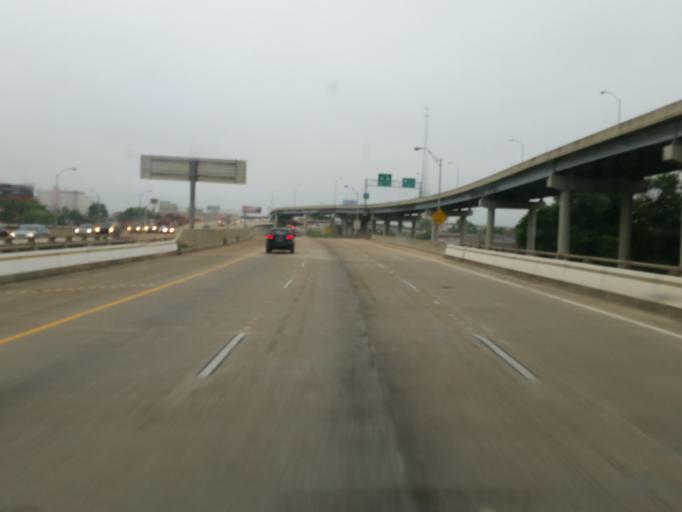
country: US
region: Louisiana
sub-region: Bossier Parish
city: Bossier City
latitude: 32.5047
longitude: -93.7464
